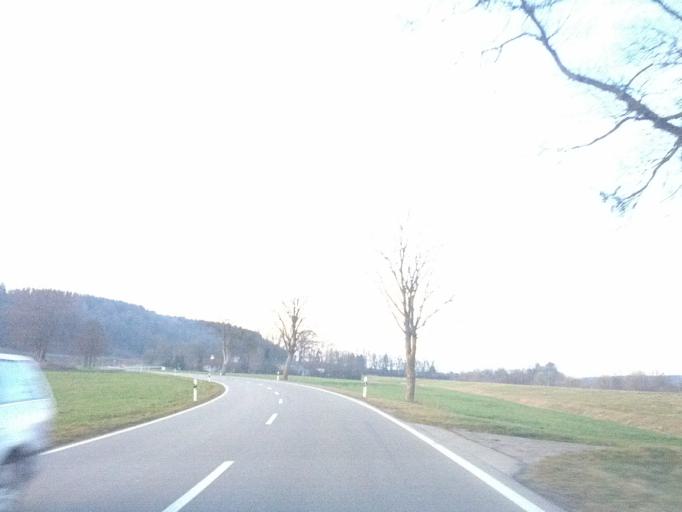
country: DE
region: Bavaria
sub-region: Swabia
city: Lautrach
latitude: 47.9076
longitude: 10.1191
